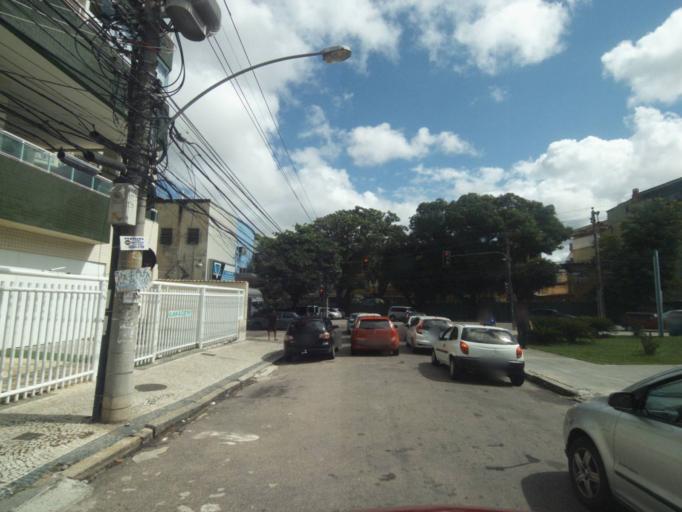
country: BR
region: Rio de Janeiro
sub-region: Sao Joao De Meriti
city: Sao Joao de Meriti
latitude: -22.9221
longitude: -43.3603
